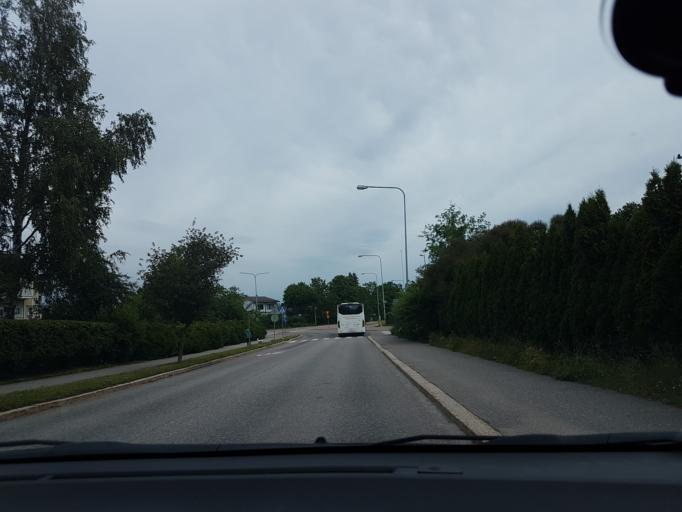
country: FI
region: Uusimaa
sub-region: Helsinki
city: Vantaa
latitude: 60.2602
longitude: 25.0023
